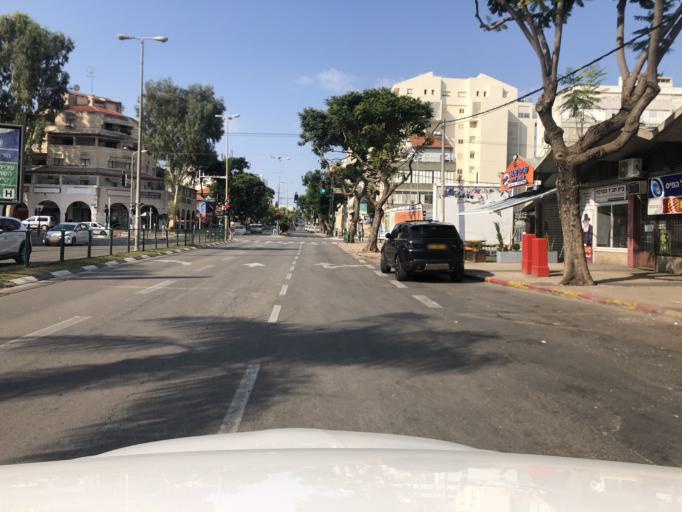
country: IL
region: Central District
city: Kfar Saba
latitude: 32.1739
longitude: 34.9148
